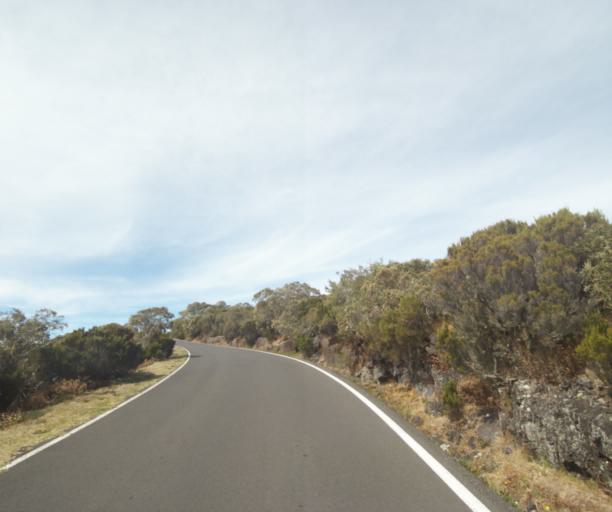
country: RE
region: Reunion
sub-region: Reunion
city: Trois-Bassins
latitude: -21.0716
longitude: 55.3834
